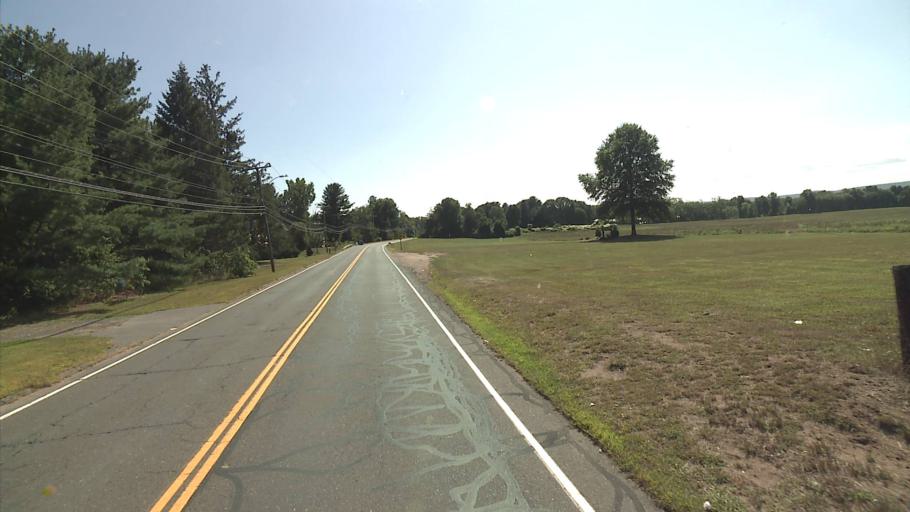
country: US
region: Connecticut
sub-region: Hartford County
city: Blue Hills
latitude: 41.8289
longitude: -72.7062
